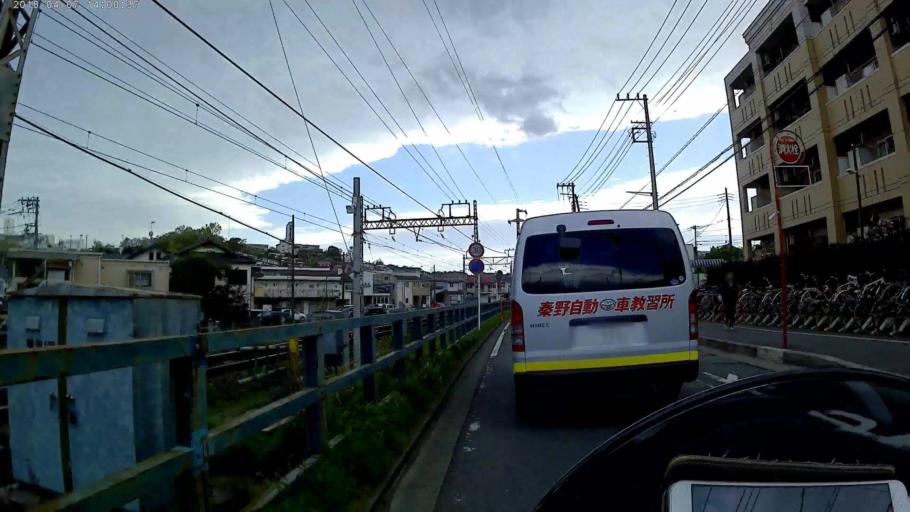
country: JP
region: Kanagawa
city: Isehara
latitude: 35.3726
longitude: 139.2704
